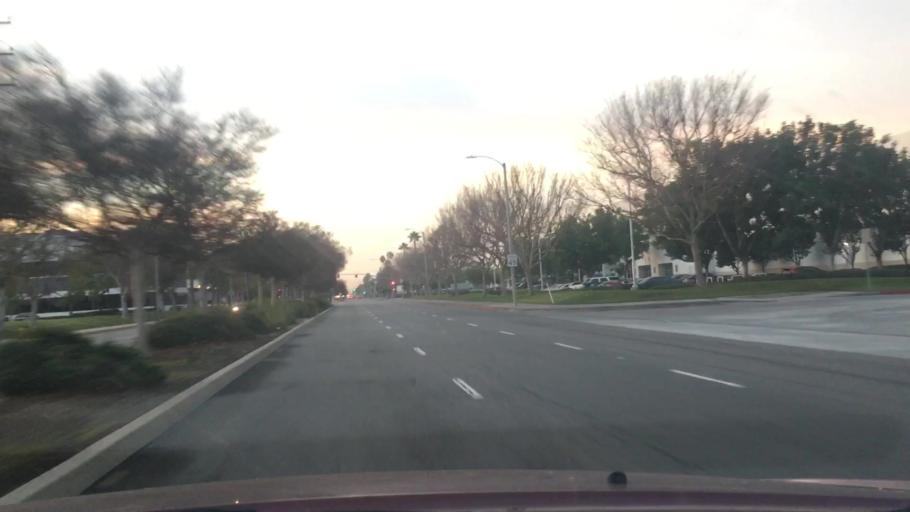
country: US
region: California
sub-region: Orange County
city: Buena Park
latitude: 33.8723
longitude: -118.0114
